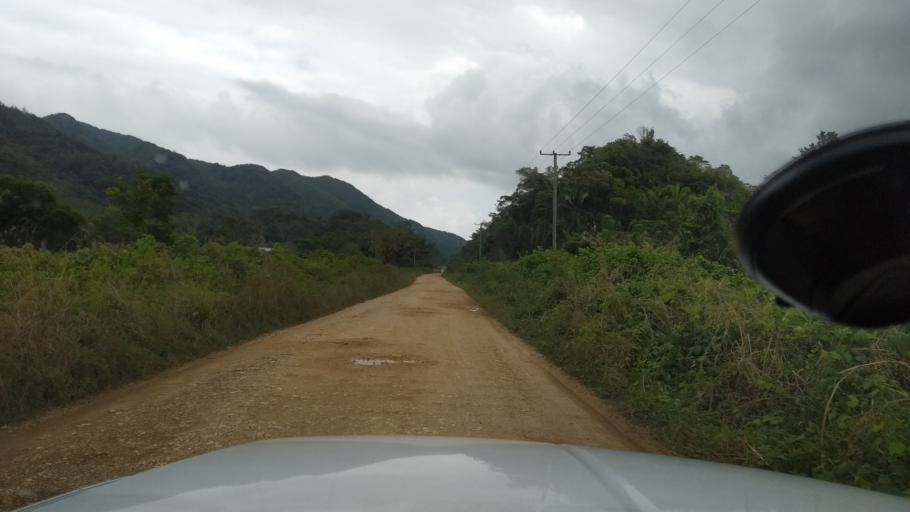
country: BZ
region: Toledo
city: Punta Gorda
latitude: 16.2047
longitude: -89.0313
